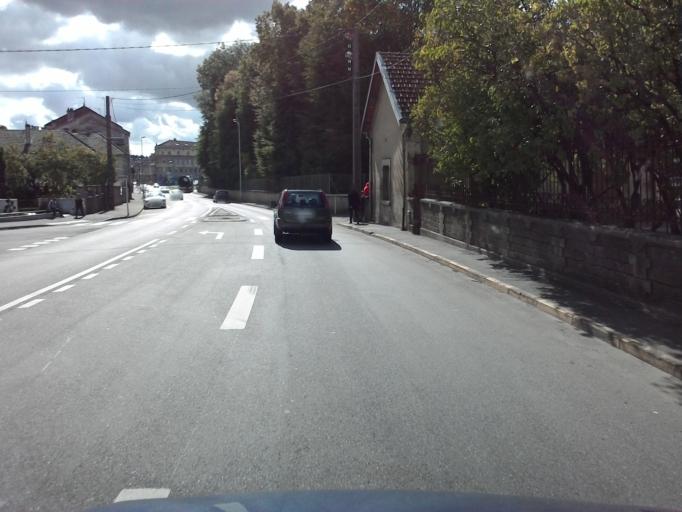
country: FR
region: Lorraine
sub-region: Departement des Vosges
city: Neufchateau
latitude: 48.3589
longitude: 5.6926
